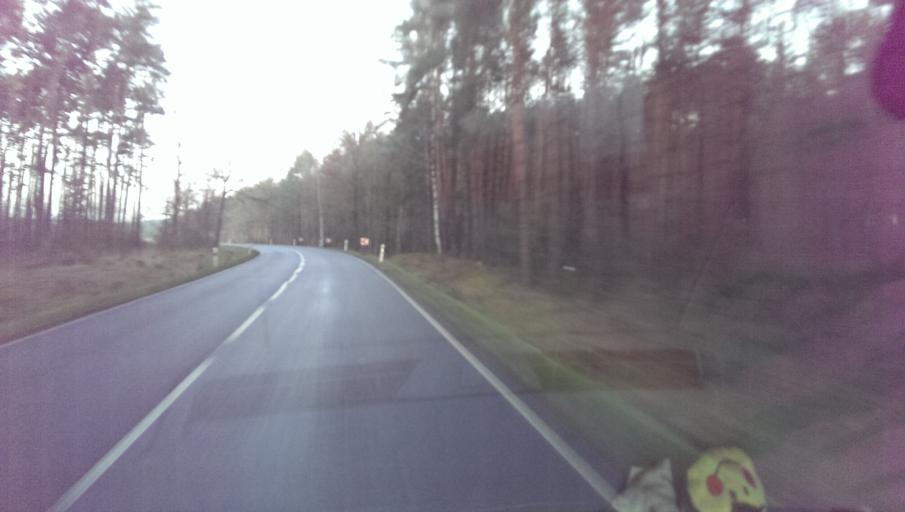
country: DE
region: Saxony-Anhalt
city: Holzdorf
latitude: 51.8500
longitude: 13.1473
